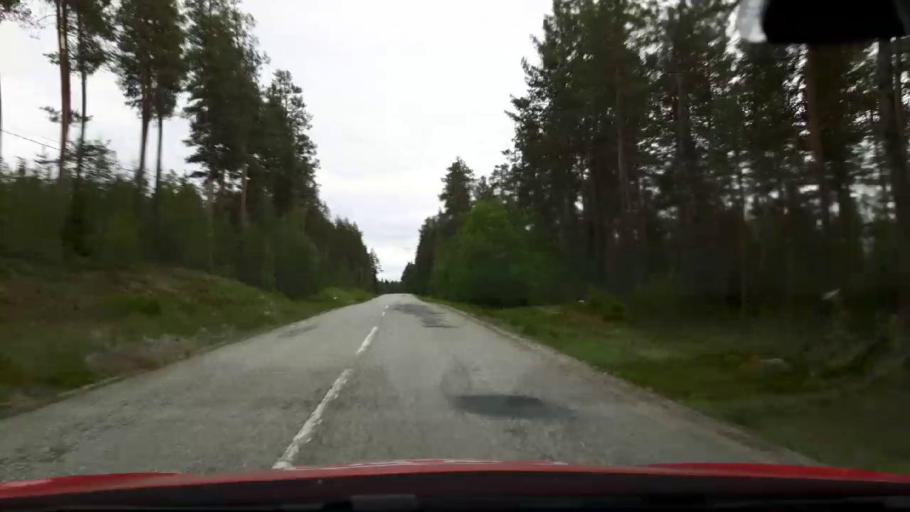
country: SE
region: Jaemtland
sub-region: Ragunda Kommun
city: Hammarstrand
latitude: 63.2479
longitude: 15.9097
